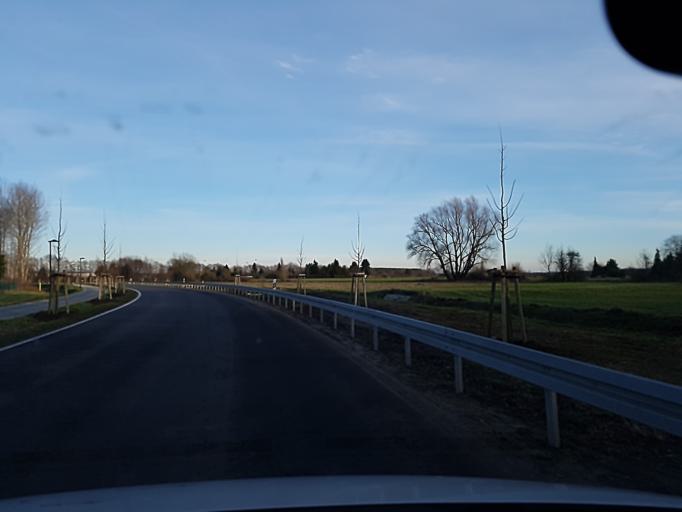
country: DE
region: Brandenburg
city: Finsterwalde
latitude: 51.6271
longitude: 13.7219
